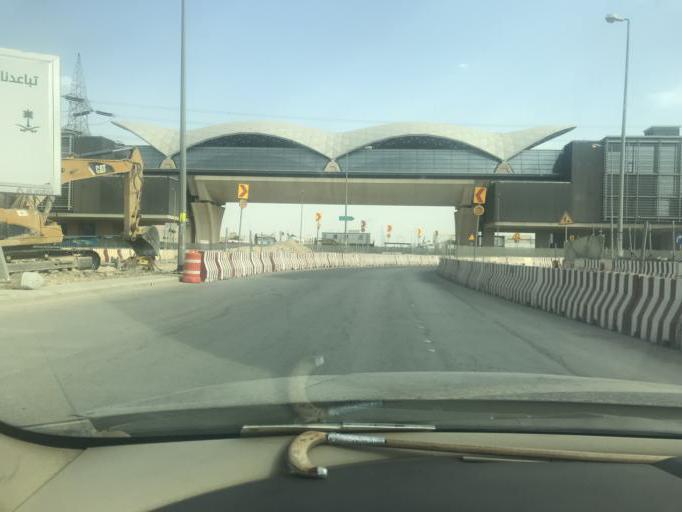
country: SA
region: Ar Riyad
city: Riyadh
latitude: 24.8023
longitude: 46.6956
